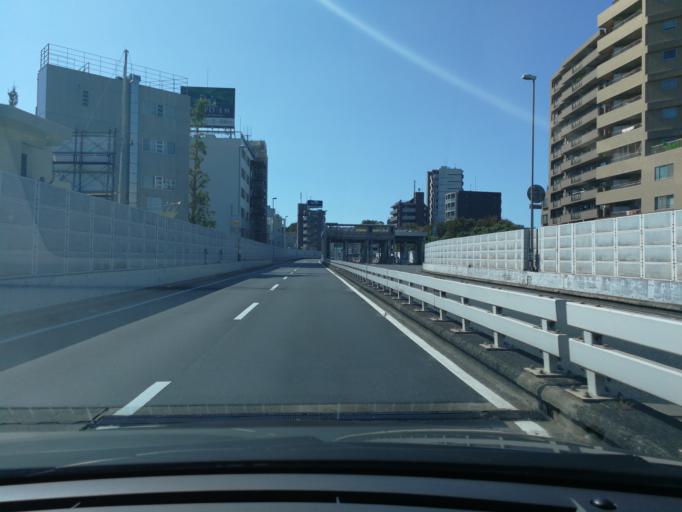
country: JP
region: Tokyo
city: Tokyo
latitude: 35.6437
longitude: 139.7213
